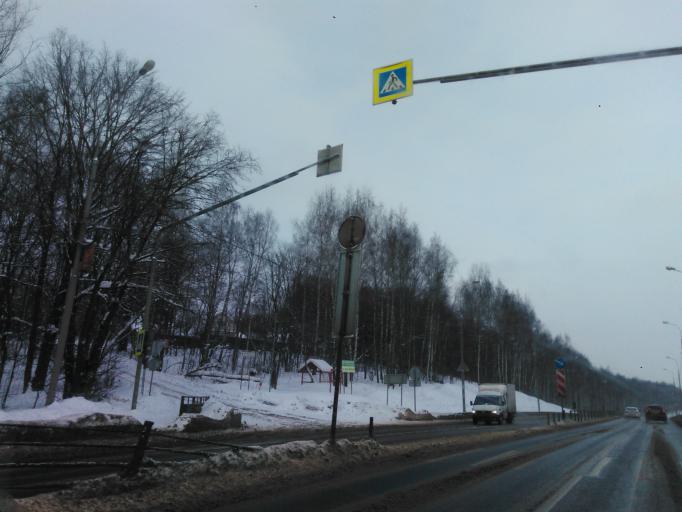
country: RU
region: Moskovskaya
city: Iksha
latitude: 56.1828
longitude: 37.5167
